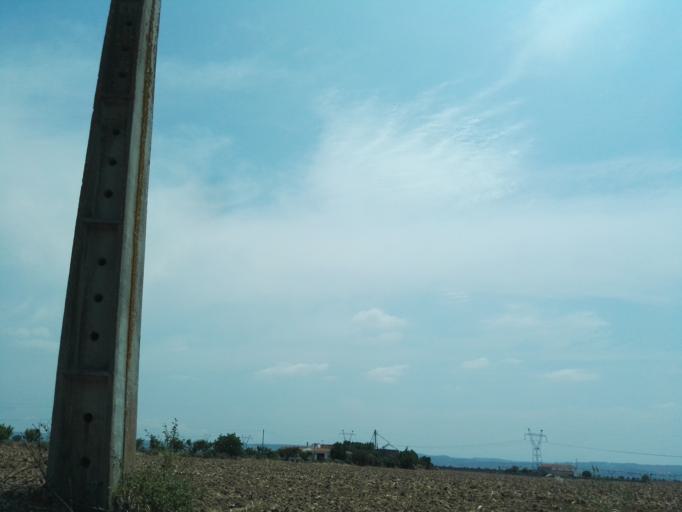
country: PT
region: Santarem
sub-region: Golega
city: Golega
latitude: 39.4269
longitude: -8.4766
